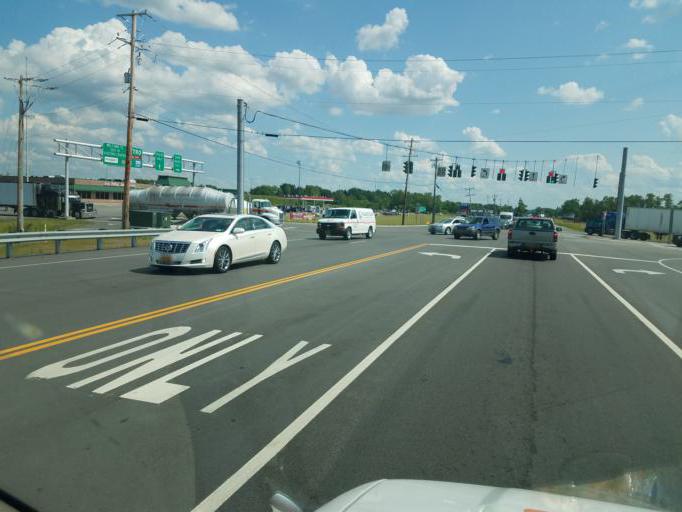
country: US
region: New York
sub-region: Seneca County
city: Waterloo
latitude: 42.9664
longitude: -76.8471
